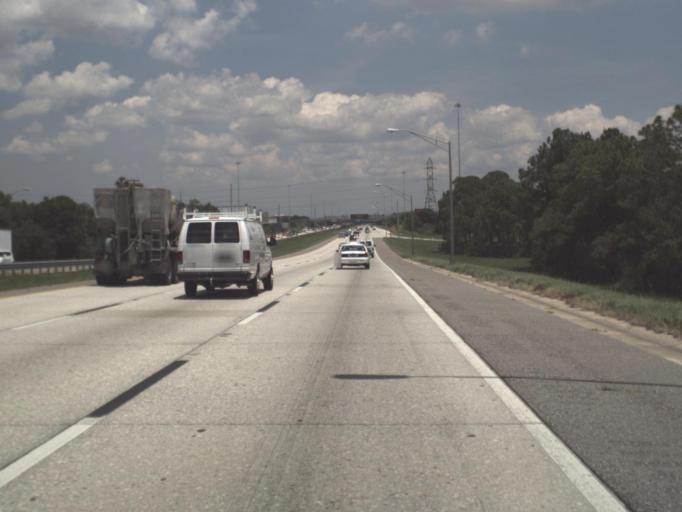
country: US
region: Florida
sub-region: Pinellas County
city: Lealman
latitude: 27.8540
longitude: -82.6637
